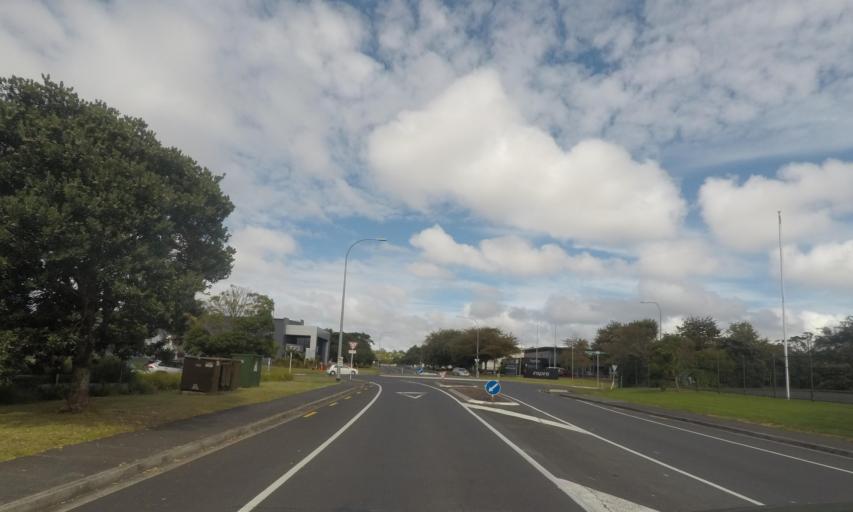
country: NZ
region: Auckland
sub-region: Auckland
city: Rothesay Bay
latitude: -36.7464
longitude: 174.6982
